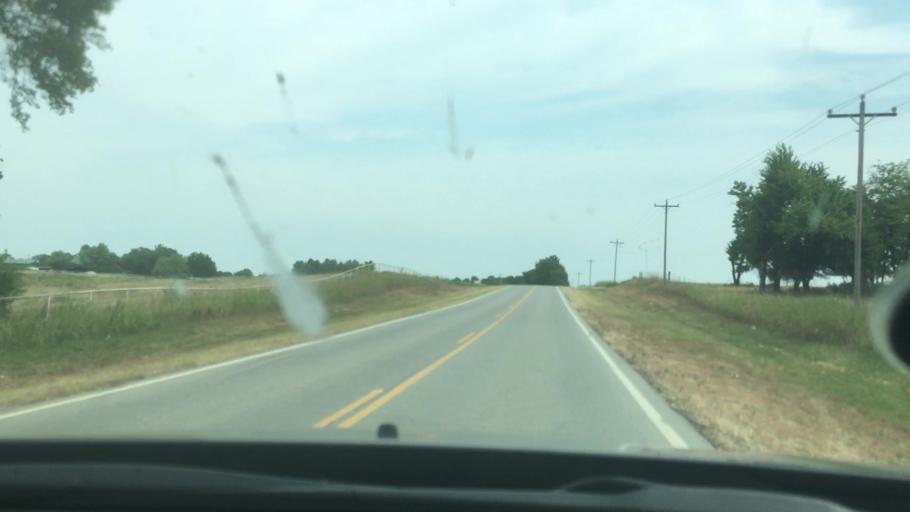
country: US
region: Oklahoma
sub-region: Coal County
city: Coalgate
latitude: 34.5737
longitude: -96.4068
